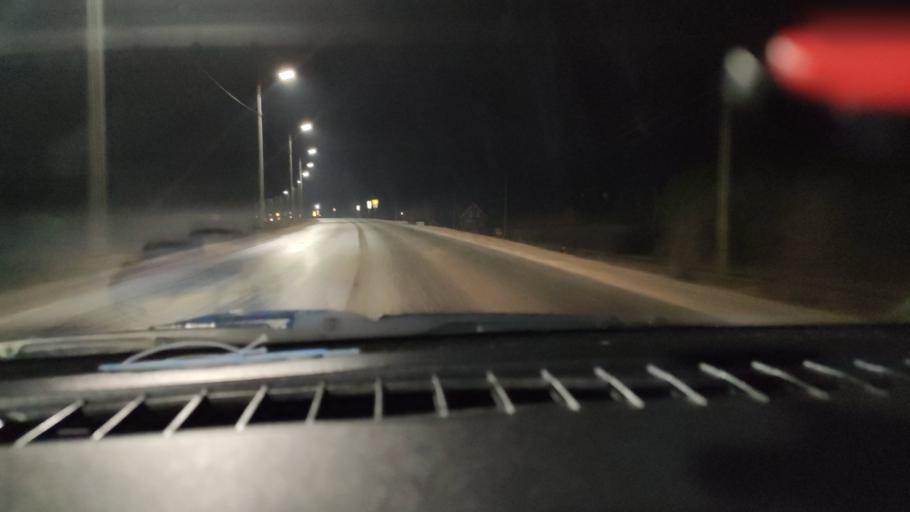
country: RU
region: Udmurtiya
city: Khokhryaki
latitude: 56.7789
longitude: 53.3635
